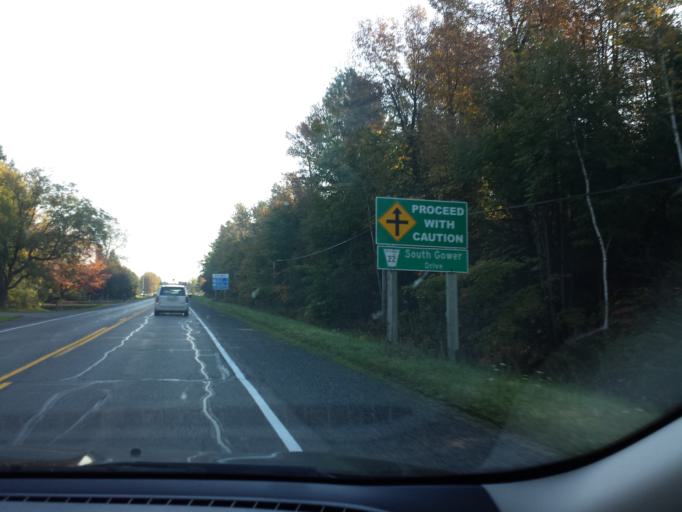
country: CA
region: Ontario
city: Prescott
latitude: 45.0375
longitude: -75.5966
